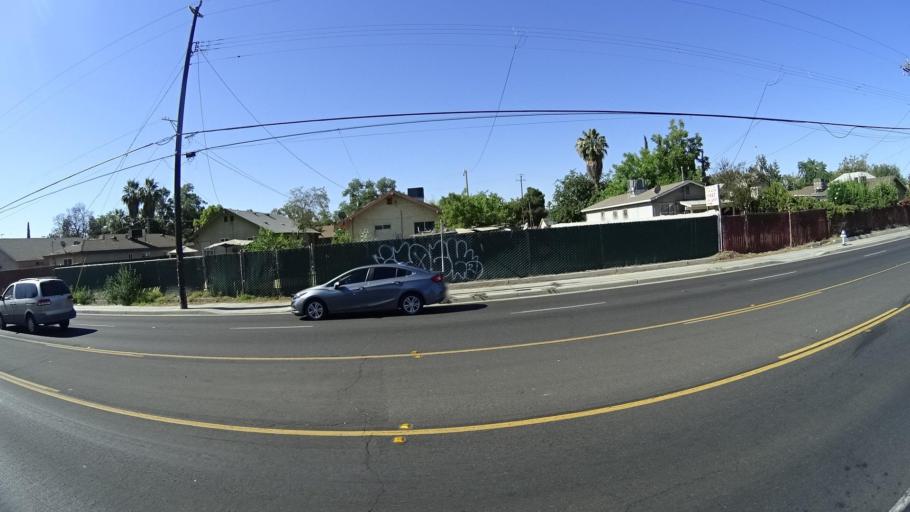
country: US
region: California
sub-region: Fresno County
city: Fresno
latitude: 36.7578
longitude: -119.7835
